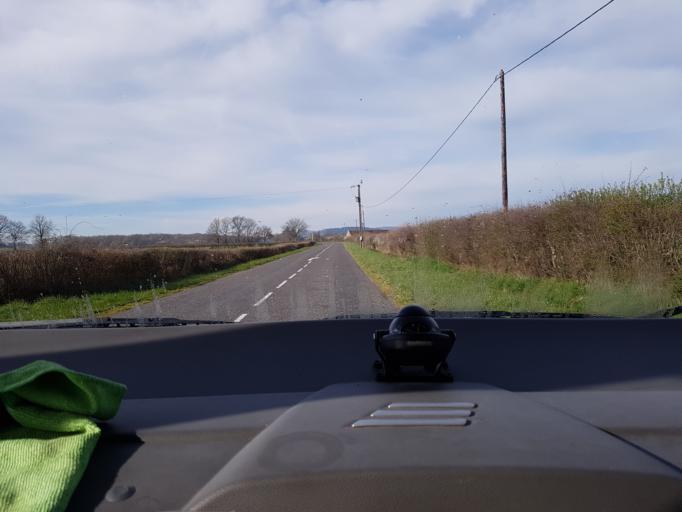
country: FR
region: Bourgogne
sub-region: Departement de Saone-et-Loire
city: Etang-sur-Arroux
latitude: 46.8203
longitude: 4.1691
